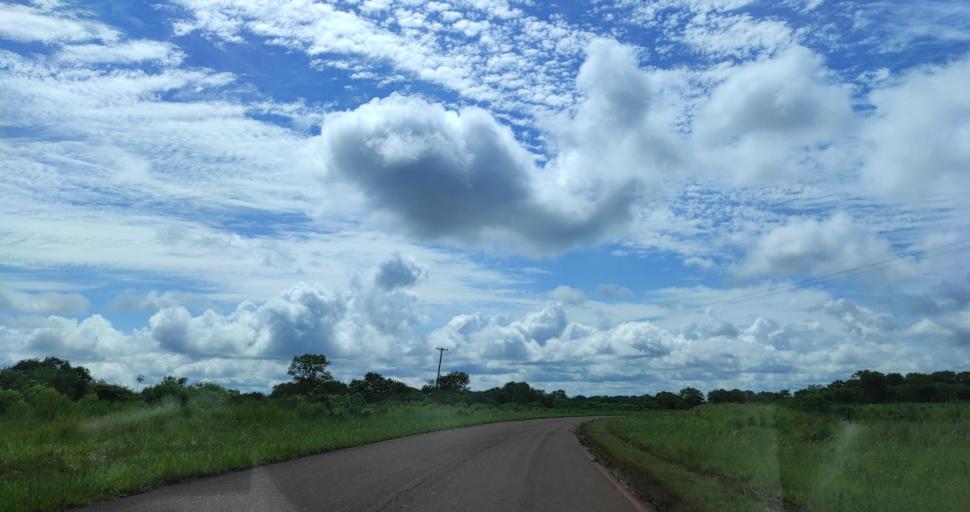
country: AR
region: Corrientes
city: San Carlos
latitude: -27.7513
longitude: -55.8730
